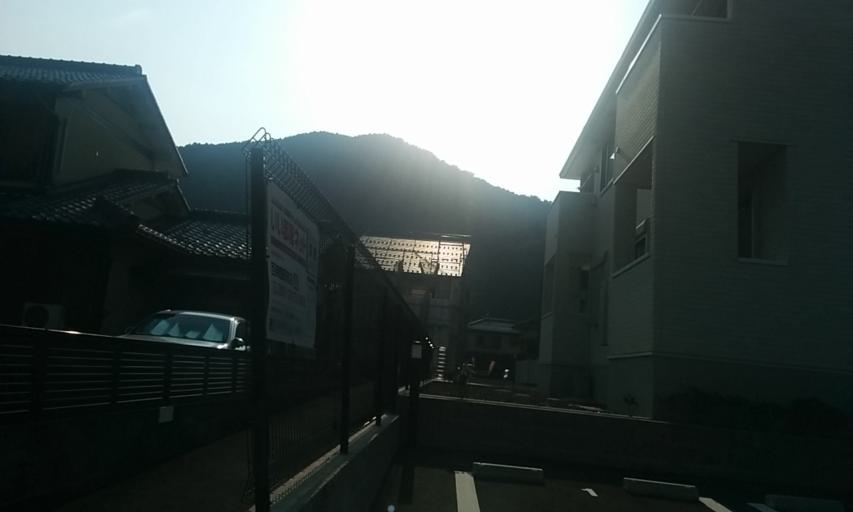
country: JP
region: Kyoto
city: Maizuru
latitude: 35.4472
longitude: 135.3263
